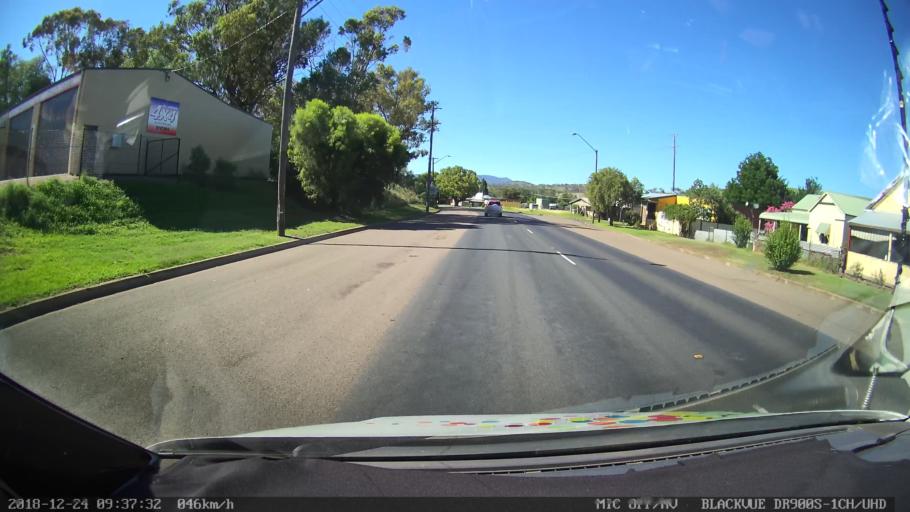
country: AU
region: New South Wales
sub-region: Liverpool Plains
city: Quirindi
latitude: -31.6458
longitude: 150.7258
